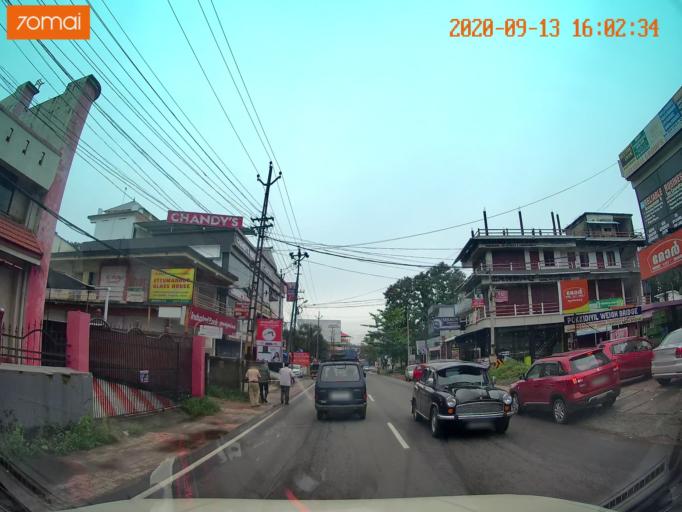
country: IN
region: Kerala
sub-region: Kottayam
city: Kottayam
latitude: 9.6712
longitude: 76.5614
